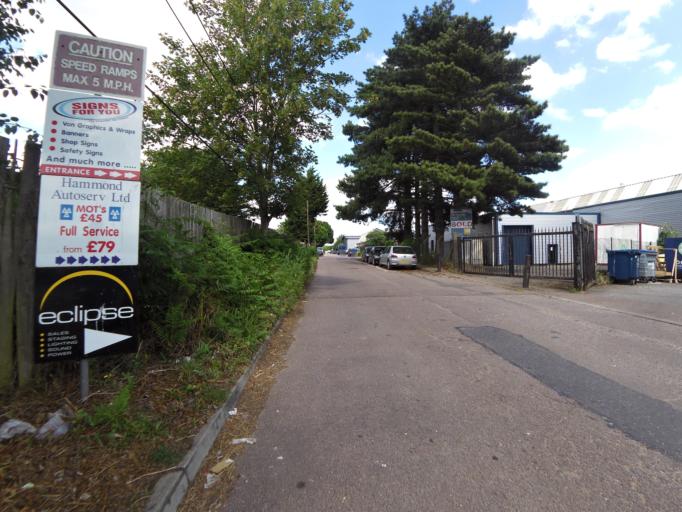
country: GB
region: England
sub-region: Suffolk
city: Kesgrave
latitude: 52.0356
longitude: 1.1979
